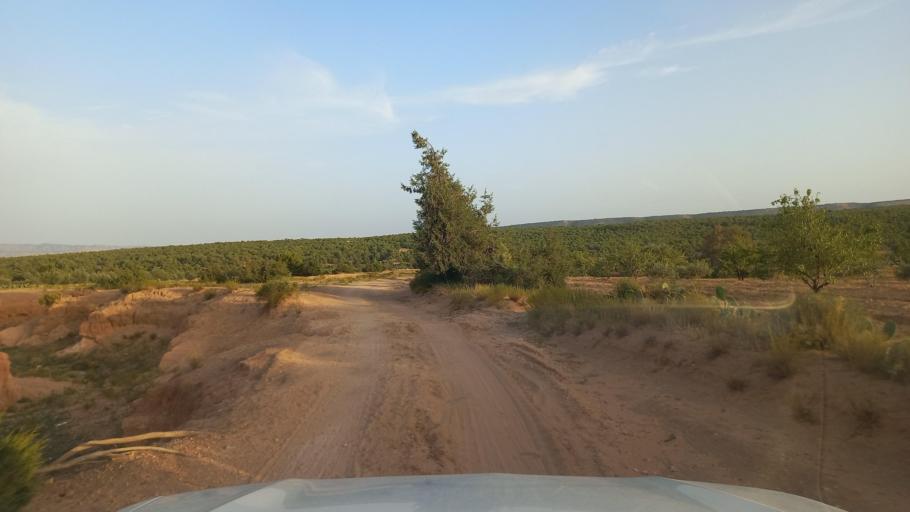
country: TN
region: Al Qasrayn
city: Sbiba
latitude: 35.4120
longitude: 8.9121
